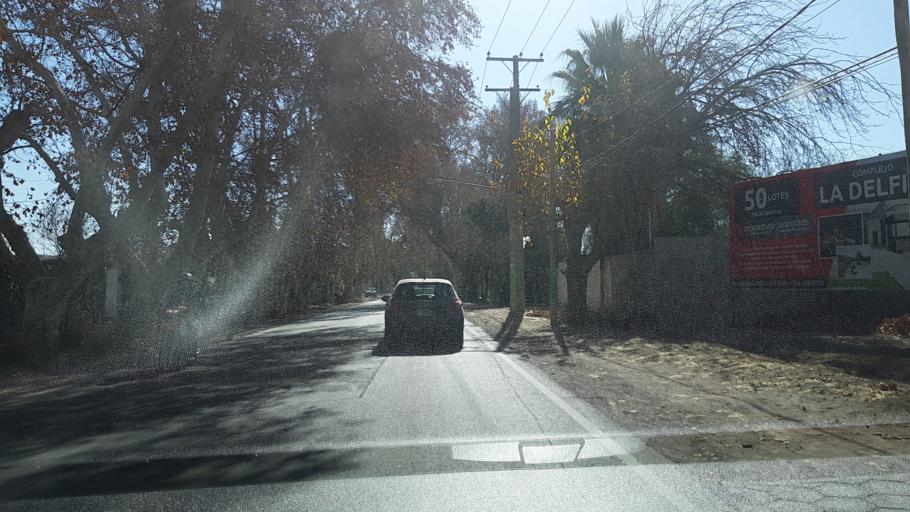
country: AR
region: San Juan
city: San Juan
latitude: -31.5265
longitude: -68.5952
